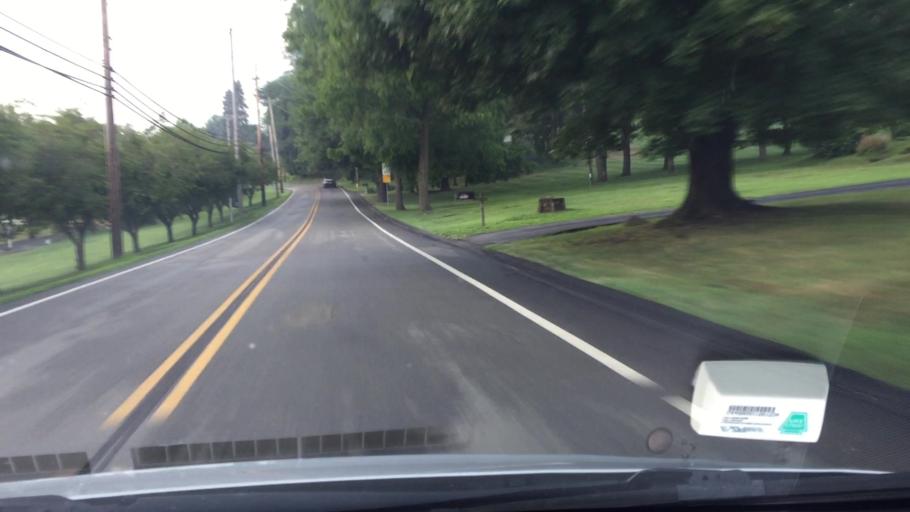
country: US
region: Pennsylvania
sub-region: Allegheny County
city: Allison Park
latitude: 40.5556
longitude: -79.9363
